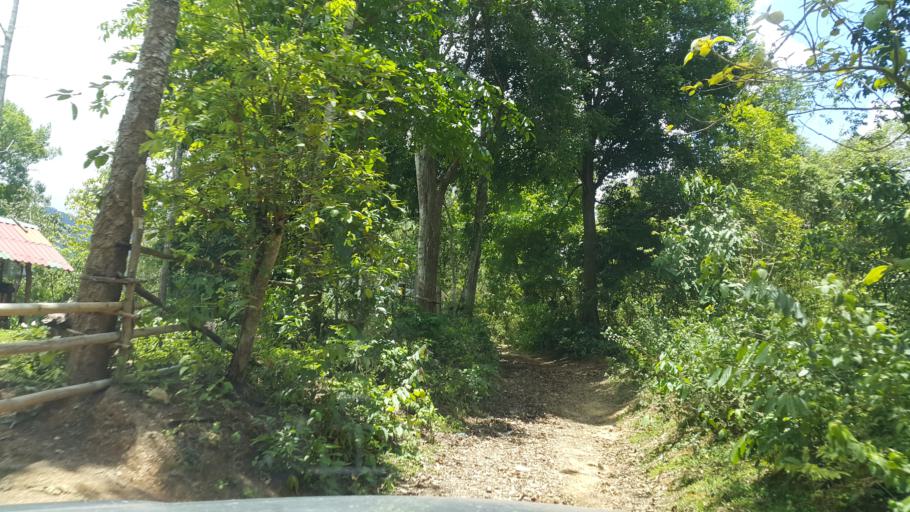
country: TH
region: Phayao
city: Phayao
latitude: 19.1798
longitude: 99.7709
